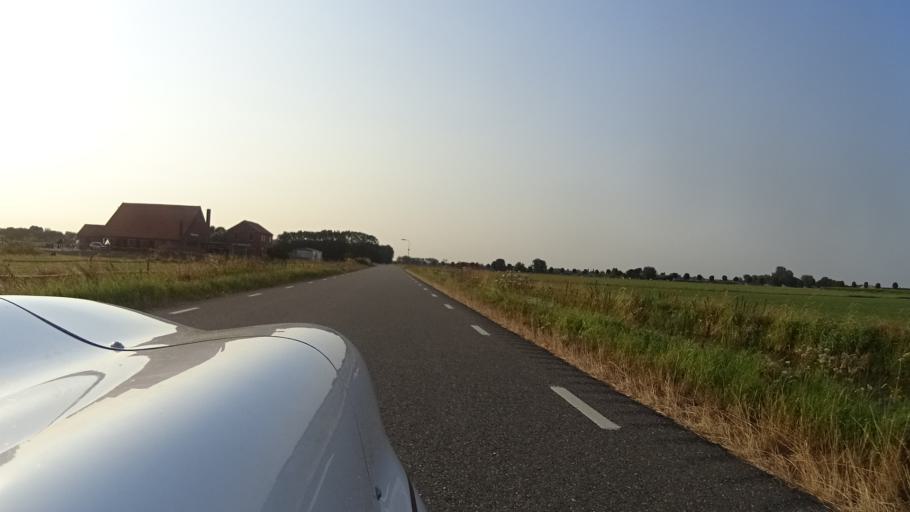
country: NL
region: North Brabant
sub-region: Gemeente Oss
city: Oss
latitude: 51.8540
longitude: 5.5211
